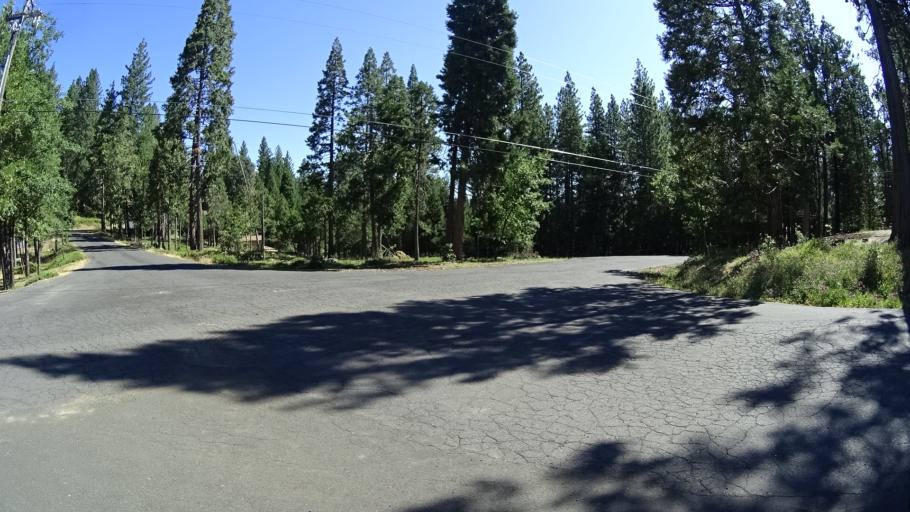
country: US
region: California
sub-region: Calaveras County
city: Arnold
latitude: 38.2487
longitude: -120.3695
